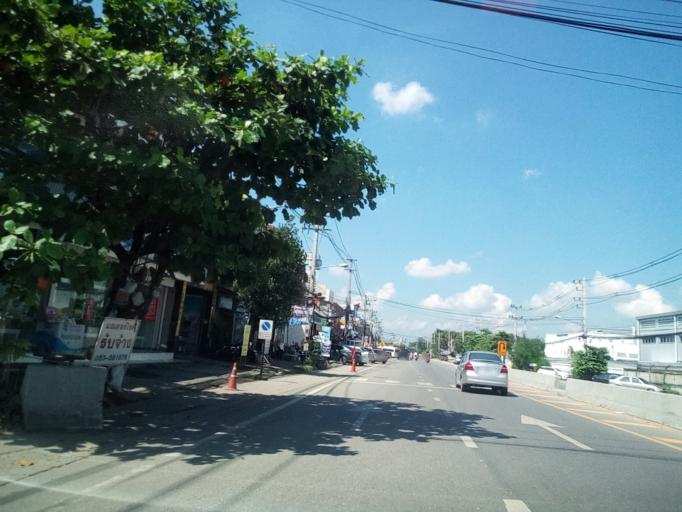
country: TH
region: Lamphun
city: Lamphun
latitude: 18.5868
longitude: 99.0501
